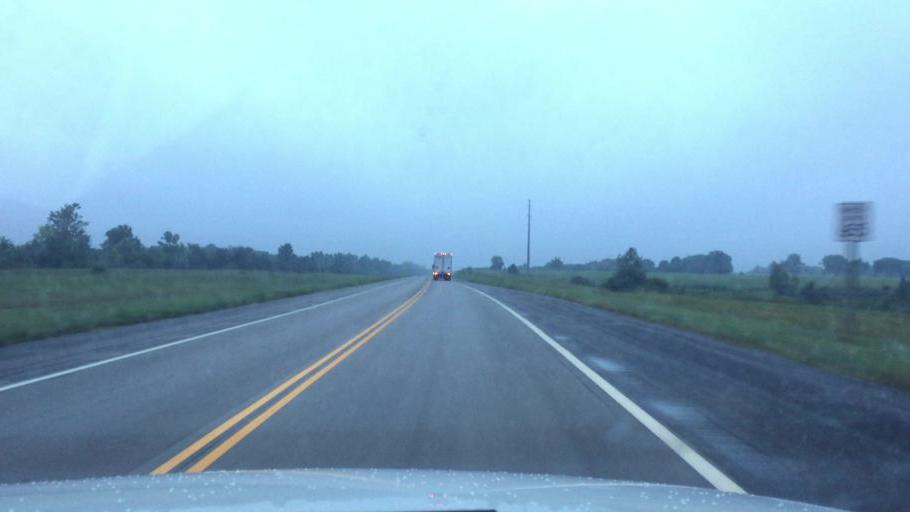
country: US
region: Kansas
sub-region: Montgomery County
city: Cherryvale
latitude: 37.4541
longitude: -95.4827
